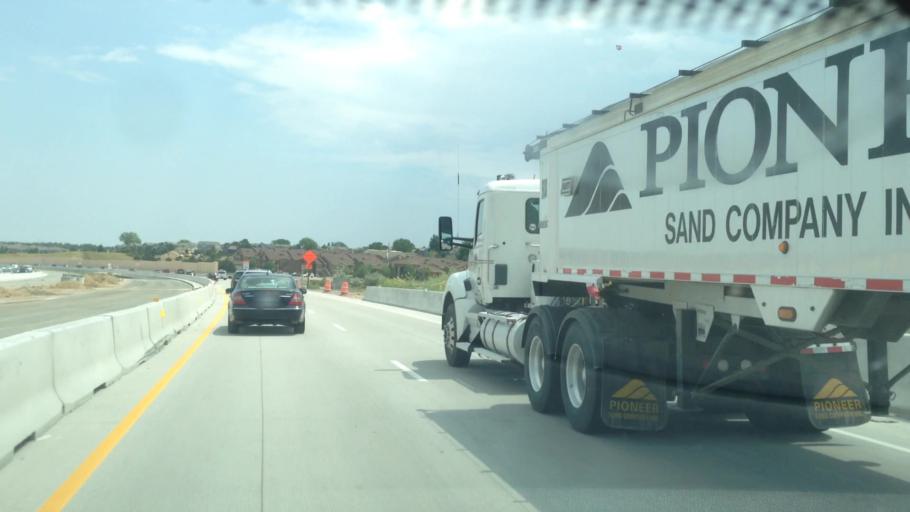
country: US
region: Colorado
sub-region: Arapahoe County
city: Southglenn
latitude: 39.5605
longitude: -104.9406
